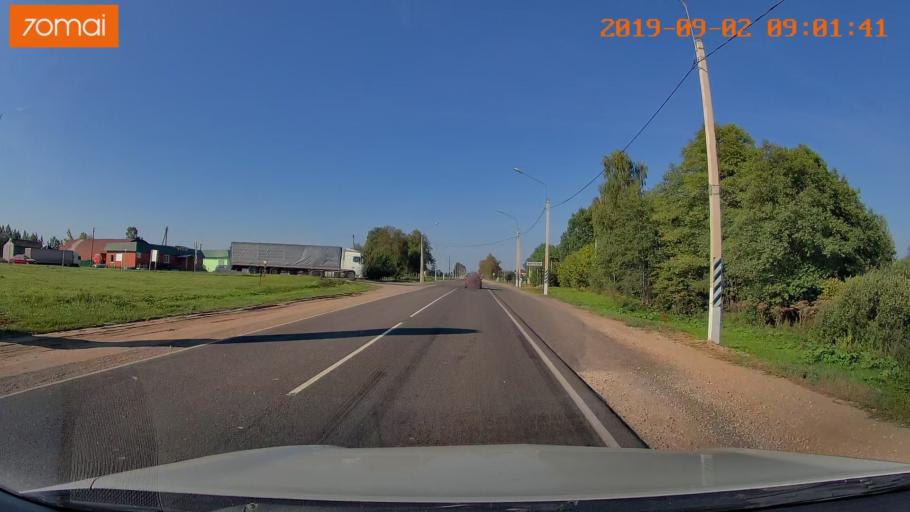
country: RU
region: Kaluga
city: Myatlevo
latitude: 54.9046
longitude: 35.6834
